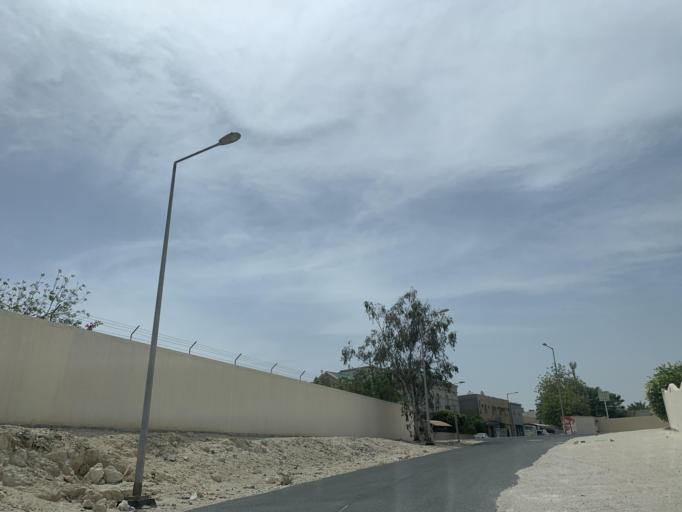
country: BH
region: Northern
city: Ar Rifa'
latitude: 26.1424
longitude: 50.5608
